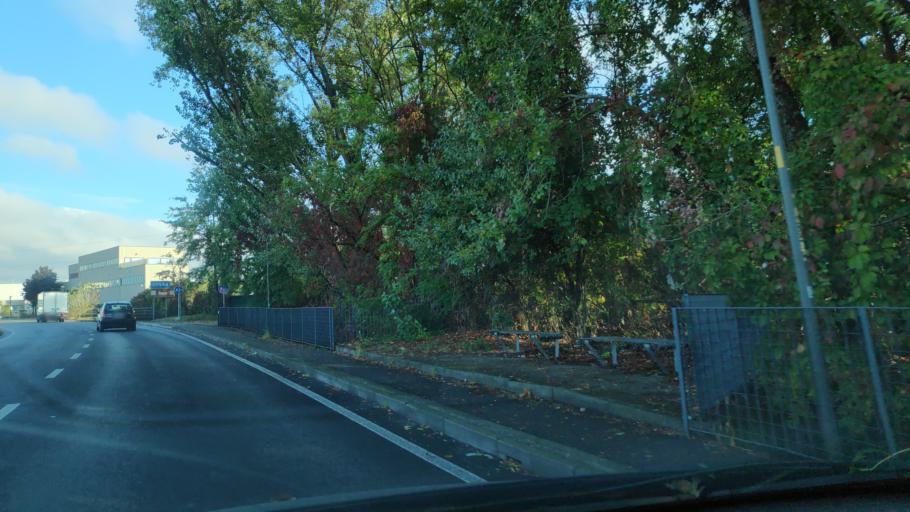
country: IT
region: Lombardy
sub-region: Citta metropolitana di Milano
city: Opera
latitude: 45.3661
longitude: 9.2178
